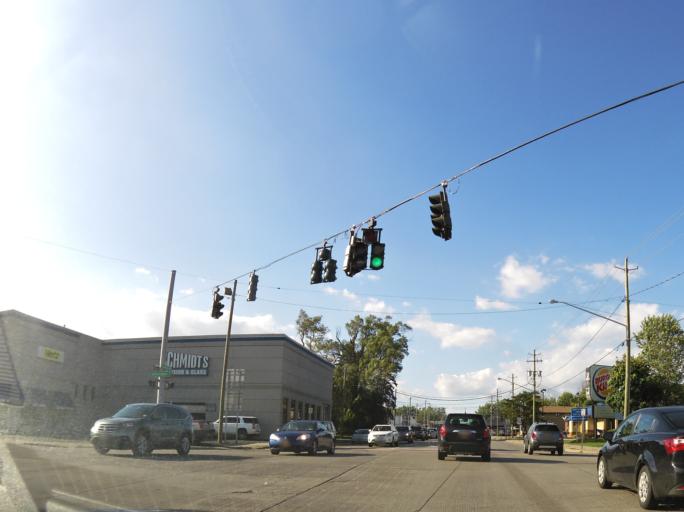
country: US
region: New York
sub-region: Erie County
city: Depew
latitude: 42.9017
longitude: -78.6970
